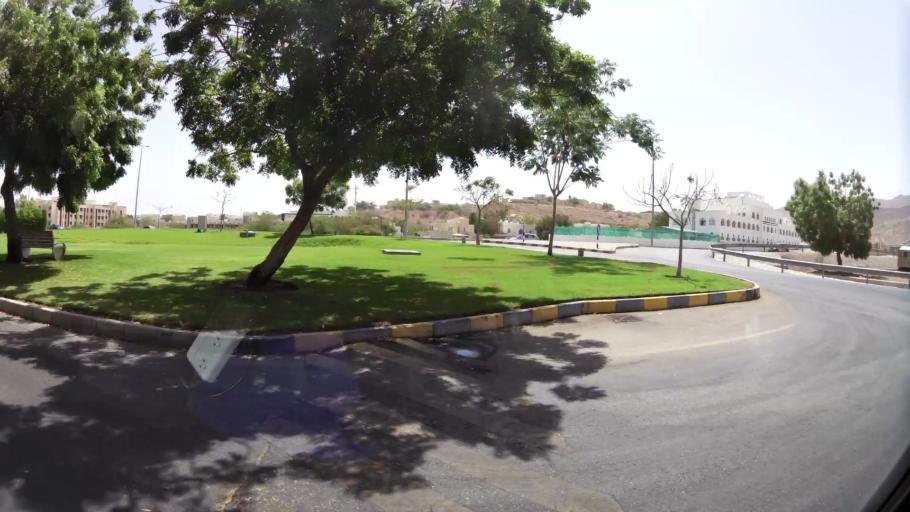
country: OM
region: Muhafazat Masqat
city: Bawshar
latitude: 23.5941
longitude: 58.4571
